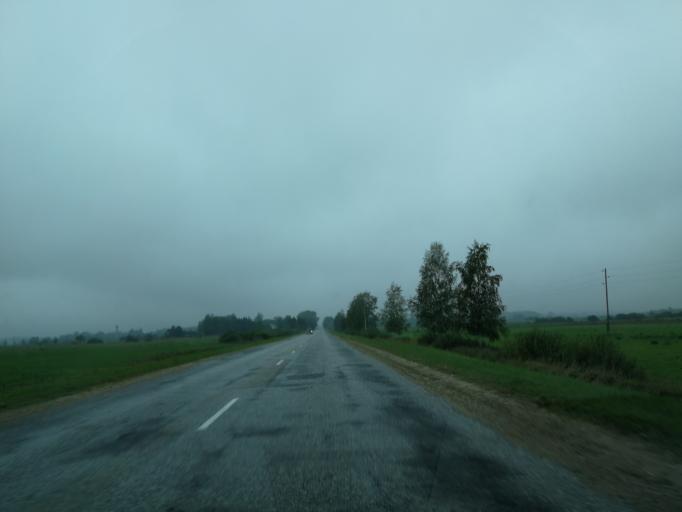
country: LV
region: Varkava
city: Vecvarkava
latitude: 56.3114
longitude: 26.5498
